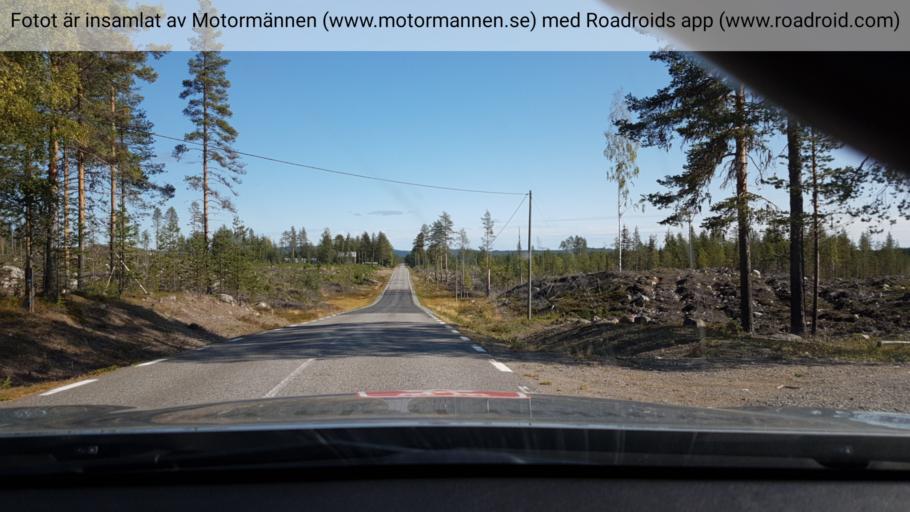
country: SE
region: Vaesterbotten
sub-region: Norsjo Kommun
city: Norsjoe
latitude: 65.1318
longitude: 19.2516
